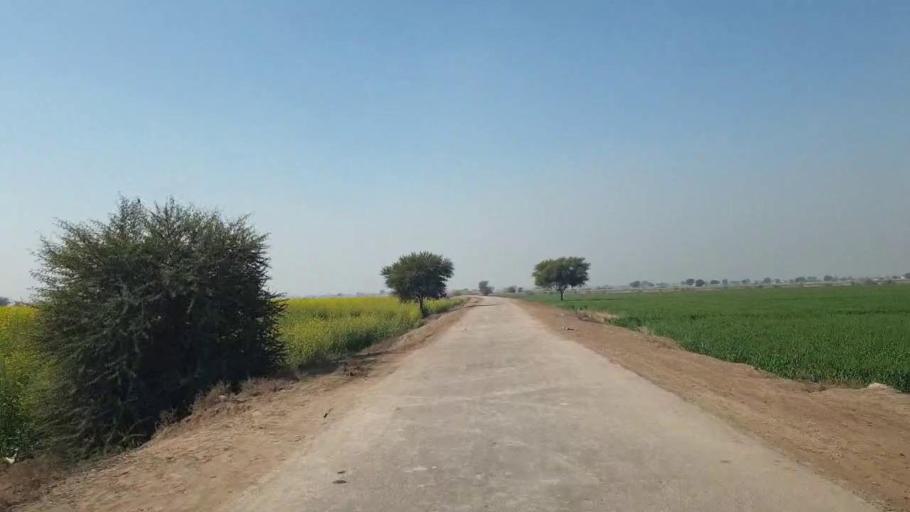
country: PK
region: Sindh
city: Shahpur Chakar
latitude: 26.1162
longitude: 68.6173
